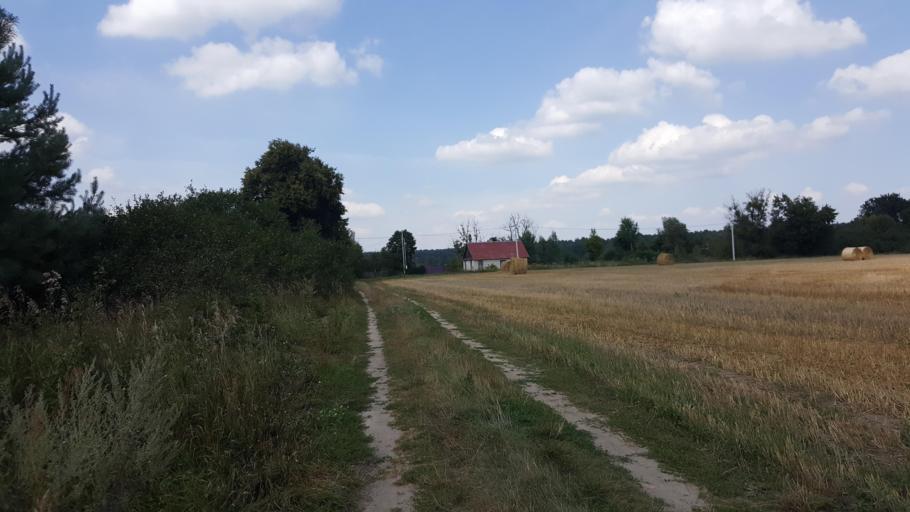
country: PL
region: Podlasie
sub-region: Powiat hajnowski
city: Hajnowka
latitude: 52.5730
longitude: 23.5583
